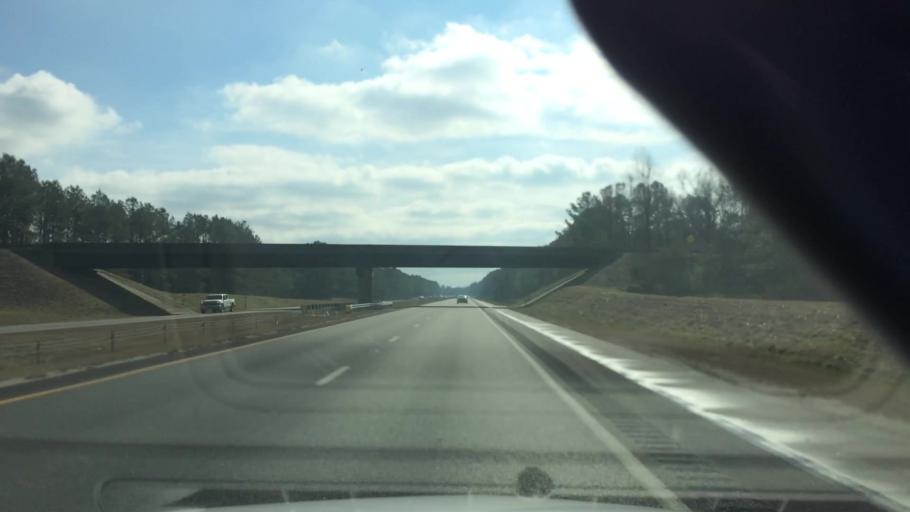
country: US
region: North Carolina
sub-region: Pender County
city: Rocky Point
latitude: 34.4802
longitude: -77.8788
